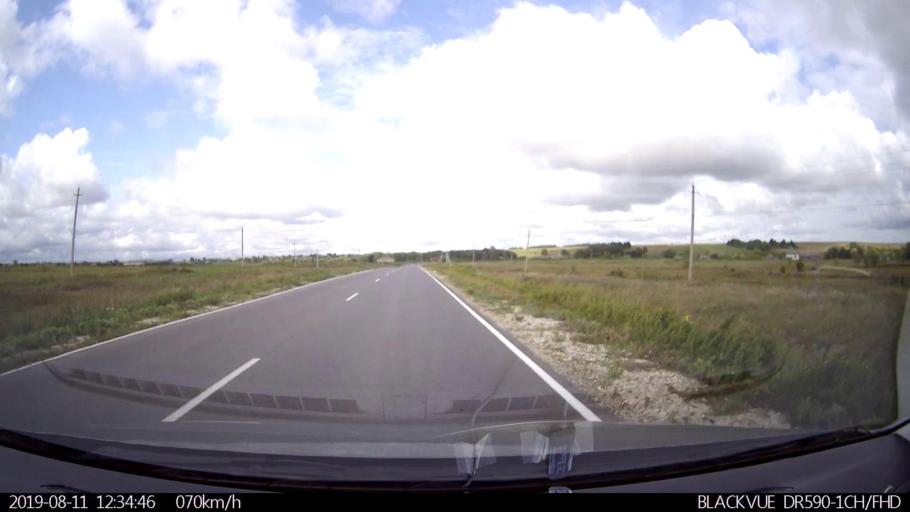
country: RU
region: Ulyanovsk
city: Ignatovka
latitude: 53.8193
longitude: 47.8385
